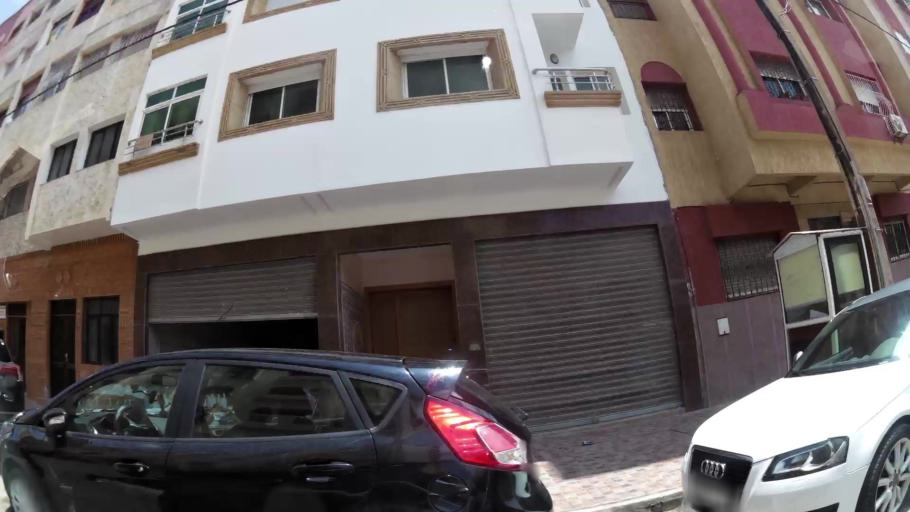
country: MA
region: Rabat-Sale-Zemmour-Zaer
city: Sale
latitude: 34.0452
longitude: -6.8227
